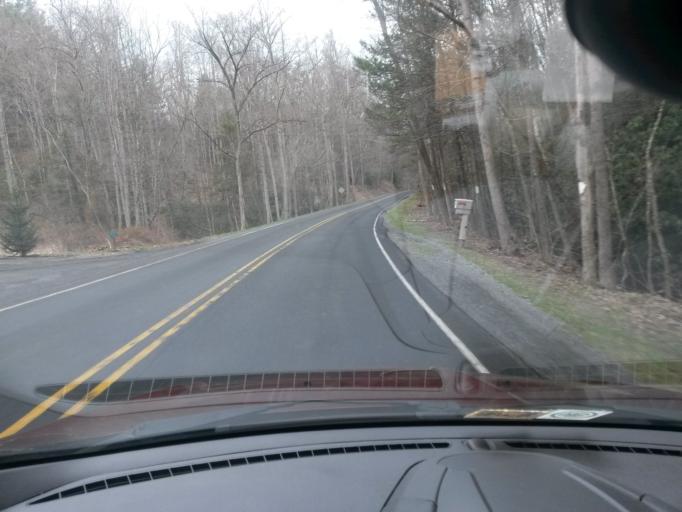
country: US
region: Virginia
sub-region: Bath County
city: Warm Springs
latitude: 38.1572
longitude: -79.7368
